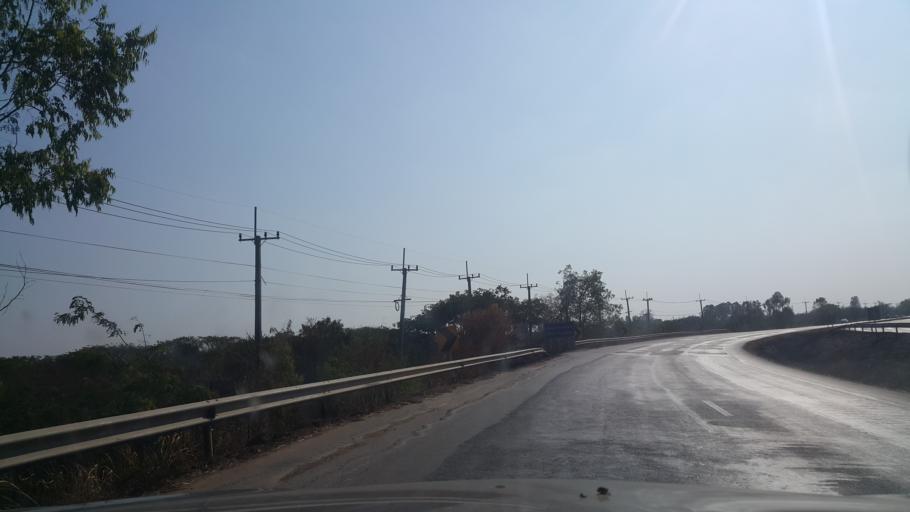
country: TH
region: Khon Kaen
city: Khon Kaen
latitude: 16.4198
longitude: 102.9165
